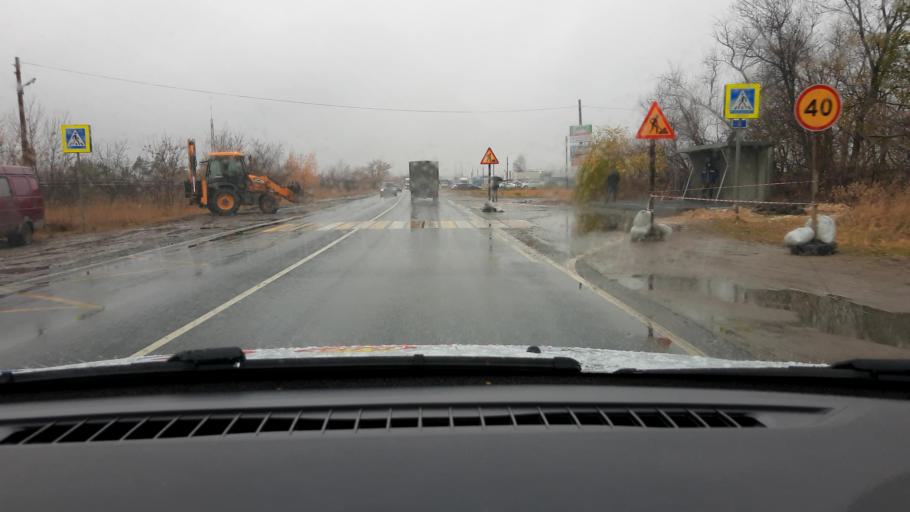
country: RU
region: Nizjnij Novgorod
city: Babino
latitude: 56.2560
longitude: 43.6047
